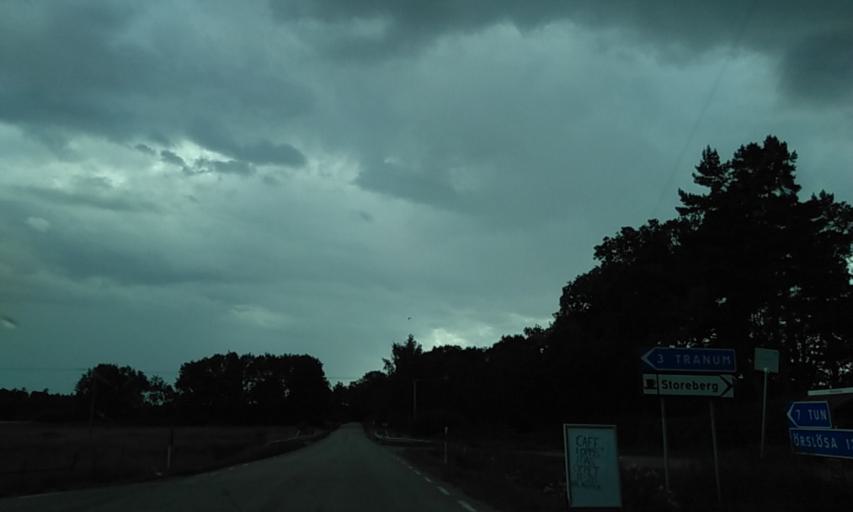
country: SE
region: Vaestra Goetaland
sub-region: Grastorps Kommun
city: Graestorp
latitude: 58.4728
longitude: 12.8236
